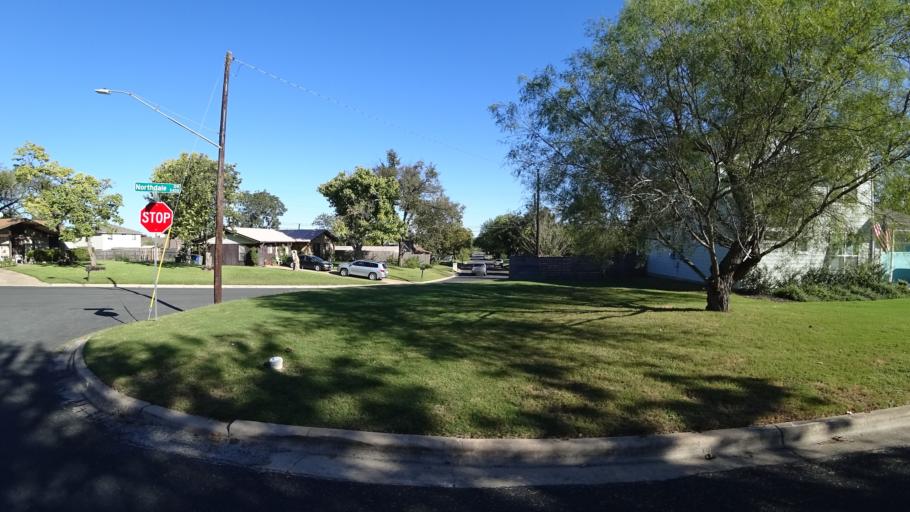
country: US
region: Texas
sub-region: Travis County
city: Austin
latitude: 30.2895
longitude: -97.6710
